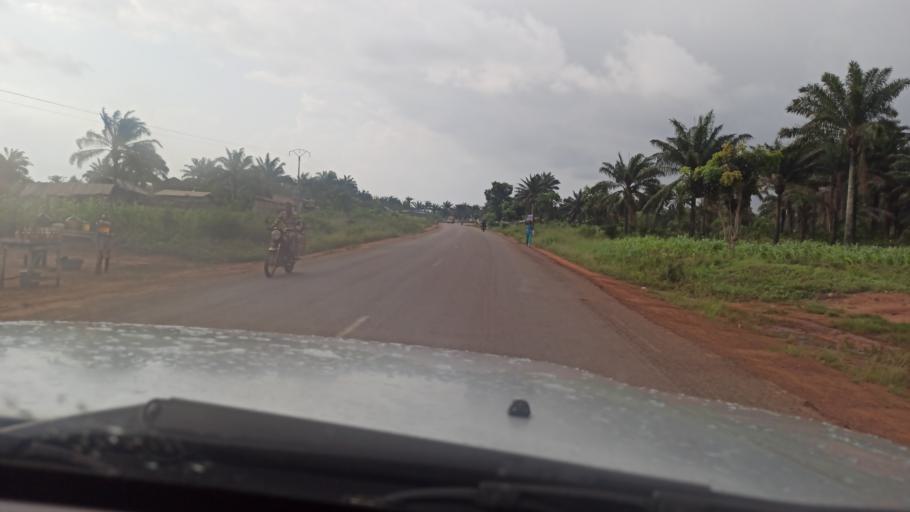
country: BJ
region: Queme
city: Porto-Novo
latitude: 6.5687
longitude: 2.5780
